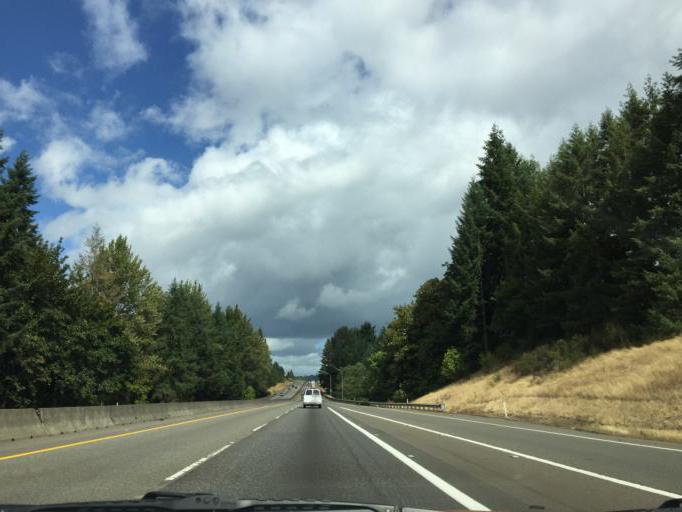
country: US
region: Washington
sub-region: Lewis County
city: Winlock
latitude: 46.4432
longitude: -122.8880
